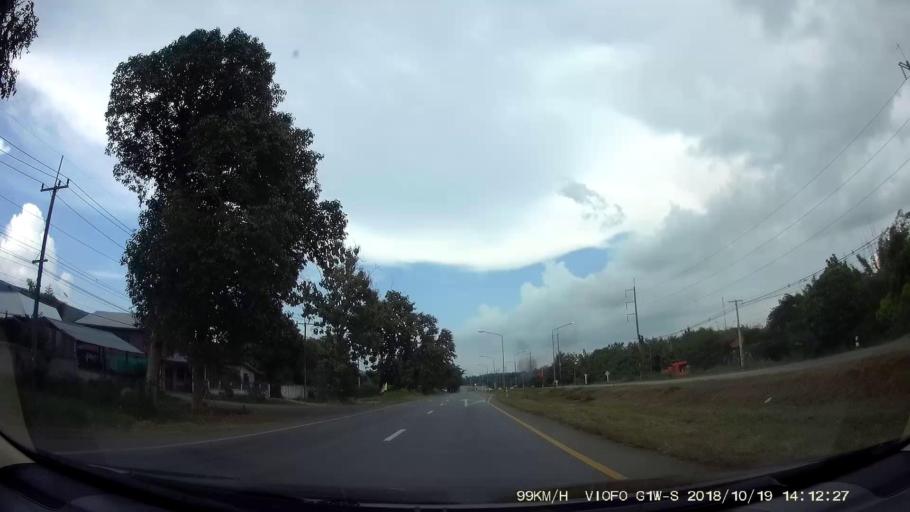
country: TH
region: Chaiyaphum
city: Khon Sawan
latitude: 15.9480
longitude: 102.1735
